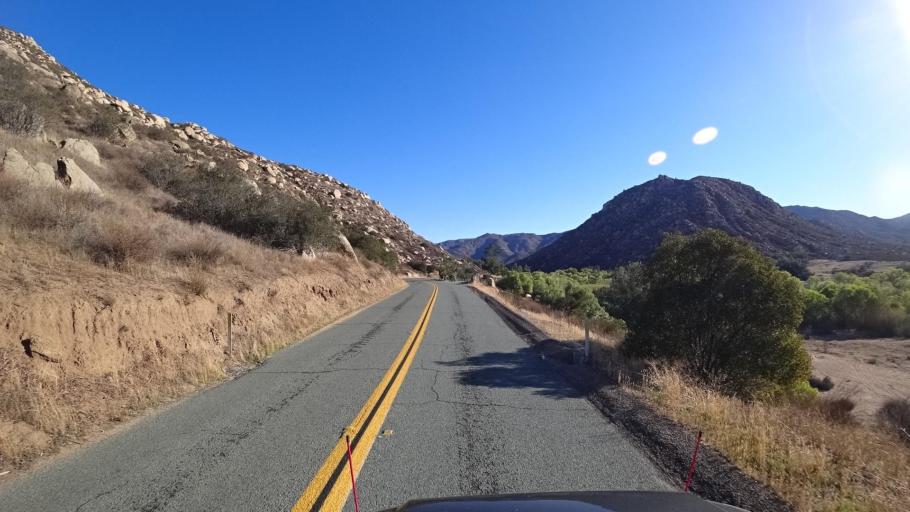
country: MX
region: Baja California
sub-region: Tecate
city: Lomas de Santa Anita
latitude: 32.6162
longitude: -116.6987
